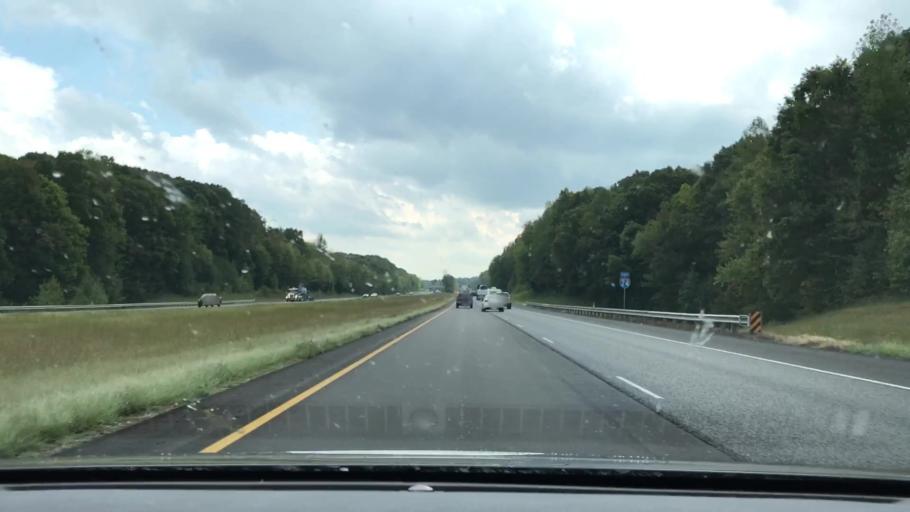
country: US
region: Tennessee
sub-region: Robertson County
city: Coopertown
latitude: 36.3438
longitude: -86.9241
